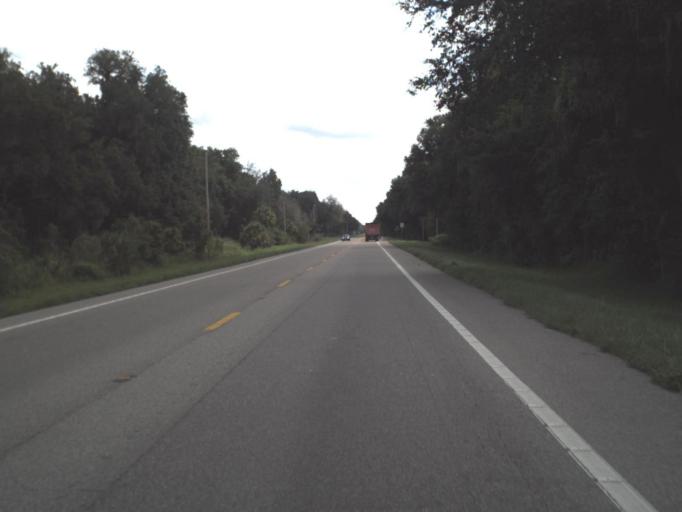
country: US
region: Florida
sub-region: Pasco County
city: Crystal Springs
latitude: 28.1339
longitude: -82.2313
